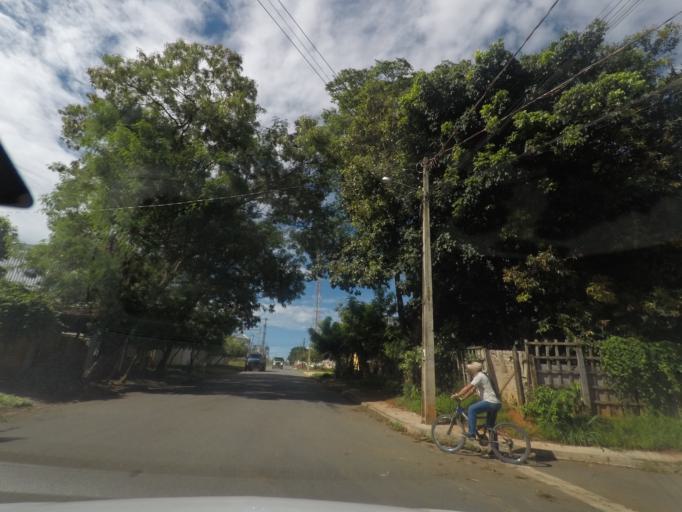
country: BR
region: Goias
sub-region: Aparecida De Goiania
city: Aparecida de Goiania
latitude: -16.7954
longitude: -49.2645
